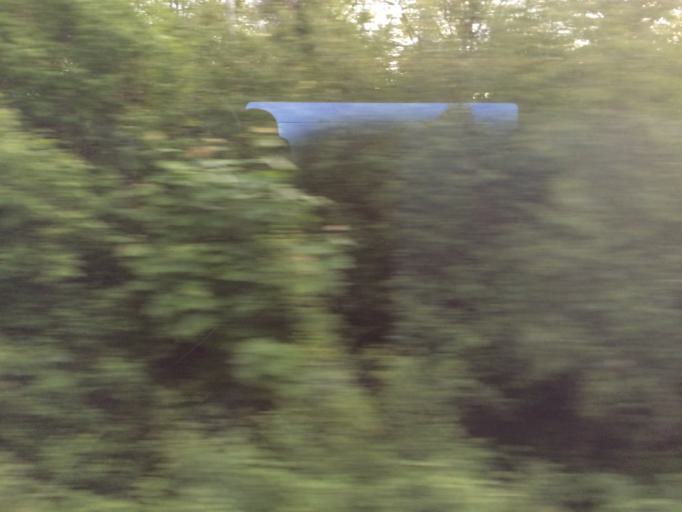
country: DE
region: North Rhine-Westphalia
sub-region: Regierungsbezirk Dusseldorf
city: Muelheim (Ruhr)
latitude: 51.4442
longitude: 6.8663
